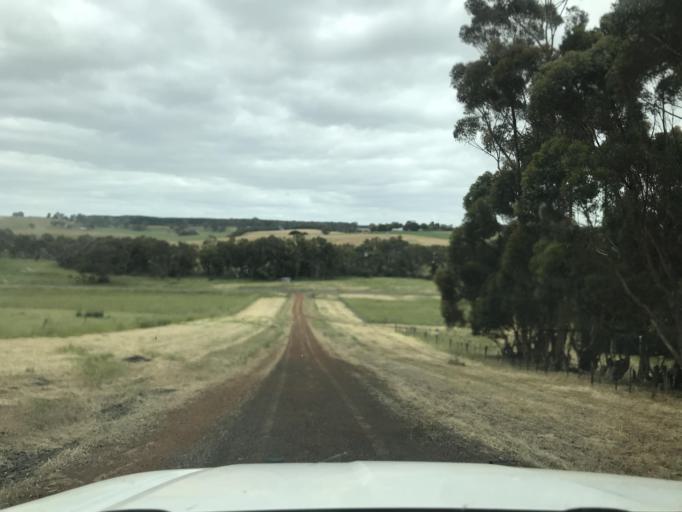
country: AU
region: South Australia
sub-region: Wattle Range
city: Penola
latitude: -37.2801
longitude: 141.4196
